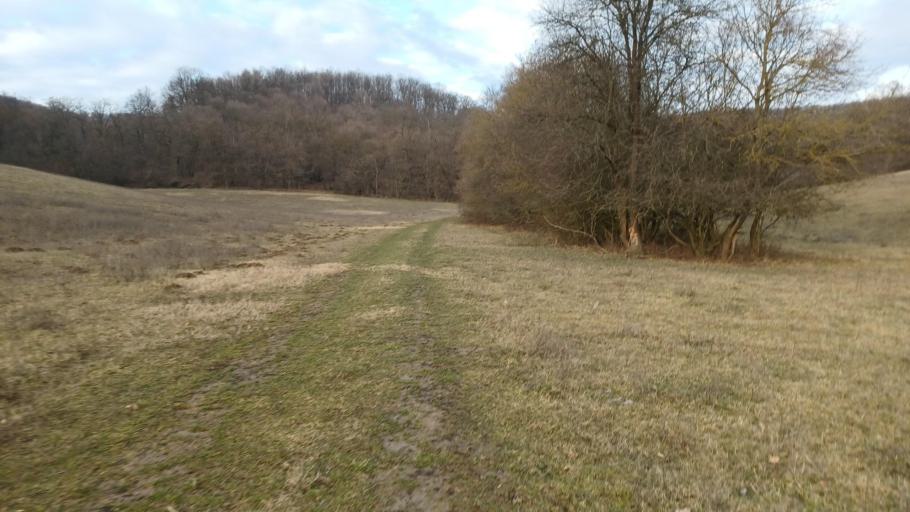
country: HU
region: Tolna
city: Szentgalpuszta
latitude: 46.3019
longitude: 18.6161
